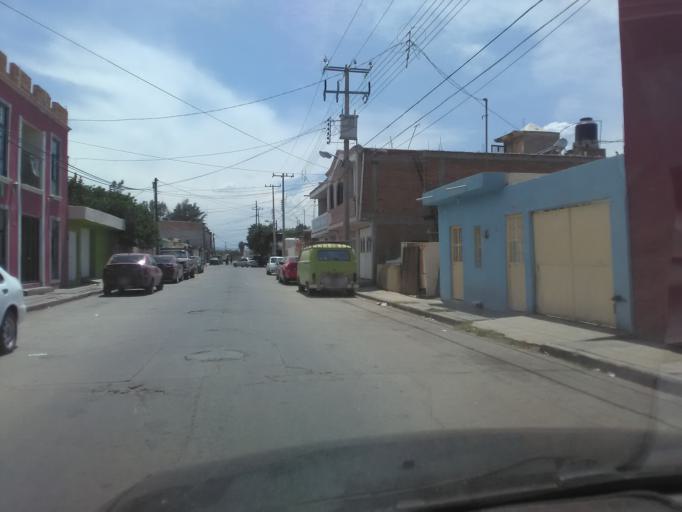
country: MX
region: Durango
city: Victoria de Durango
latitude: 24.0082
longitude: -104.6303
